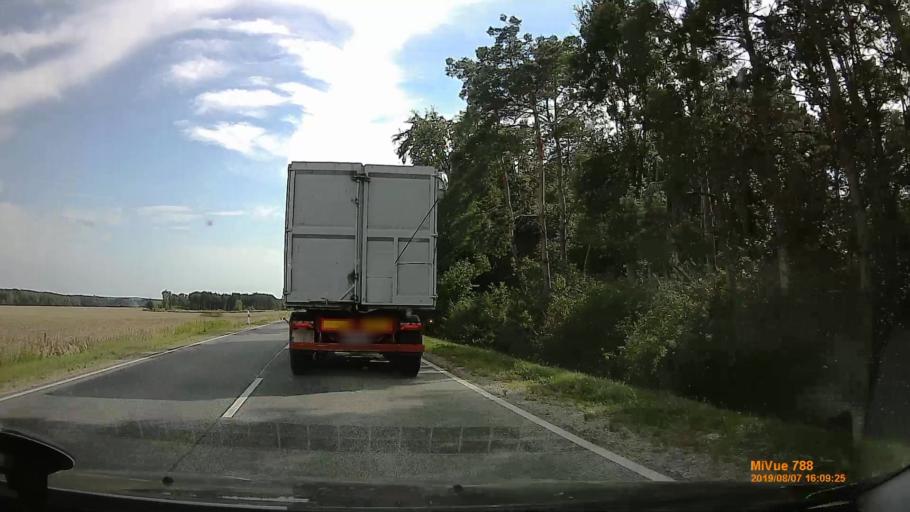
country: HU
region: Zala
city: Zalalovo
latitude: 46.8935
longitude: 16.6023
